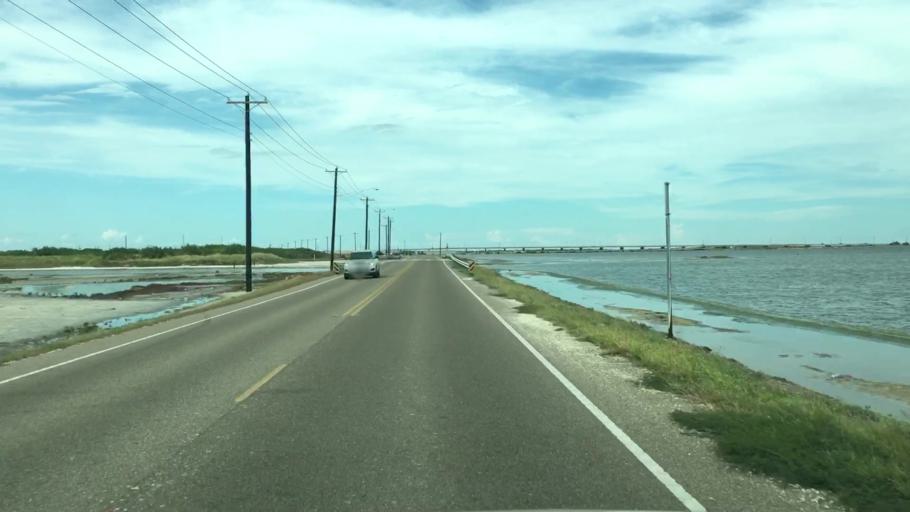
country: US
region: Texas
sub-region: Nueces County
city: Corpus Christi
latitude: 27.6508
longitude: -97.2802
